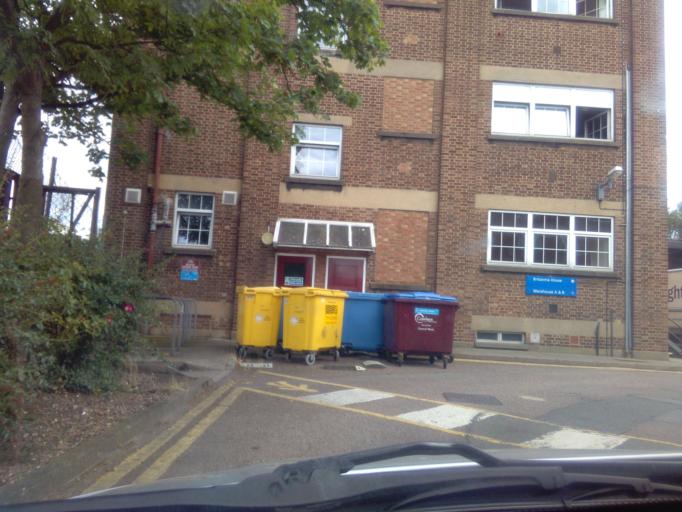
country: GB
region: England
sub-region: Bedford
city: Bedford
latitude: 52.1290
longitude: -0.4693
